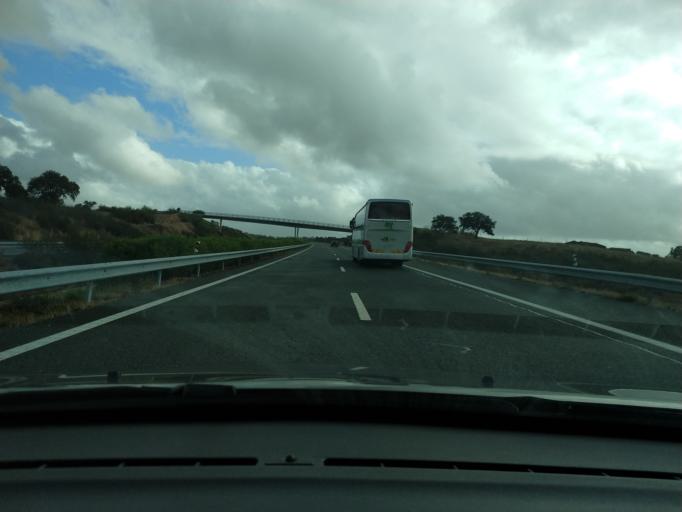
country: PT
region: Beja
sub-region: Ourique
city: Ourique
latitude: 37.5525
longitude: -8.1909
